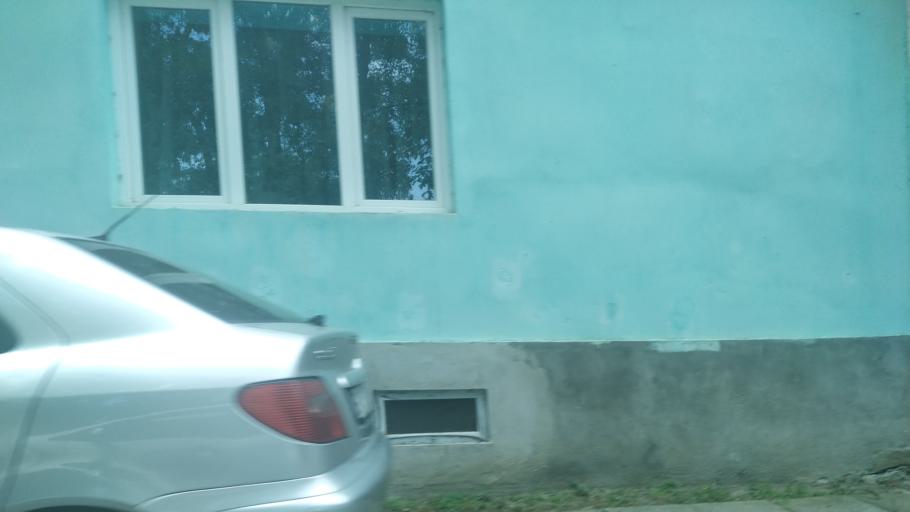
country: RO
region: Brasov
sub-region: Comuna Beclean
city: Beclean
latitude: 45.8300
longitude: 24.9242
